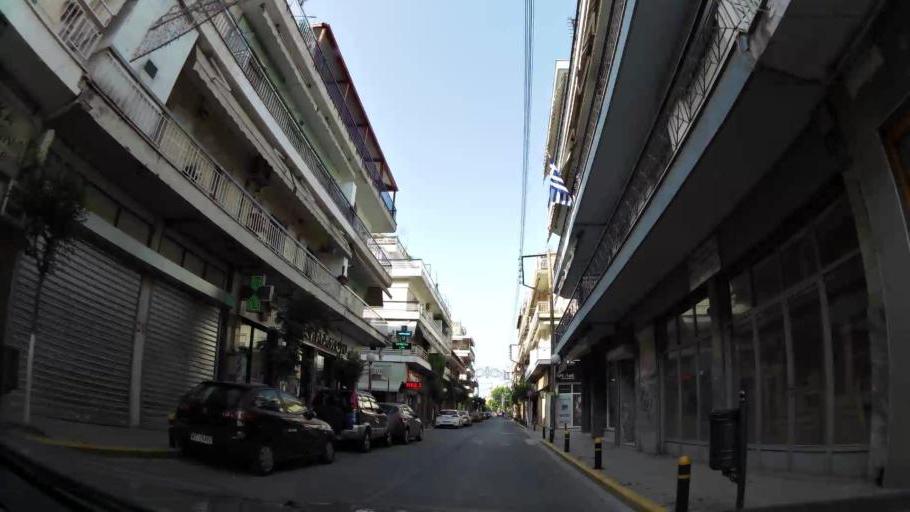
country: GR
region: Central Macedonia
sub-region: Nomos Thessalonikis
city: Ampelokipoi
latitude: 40.6561
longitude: 22.9123
